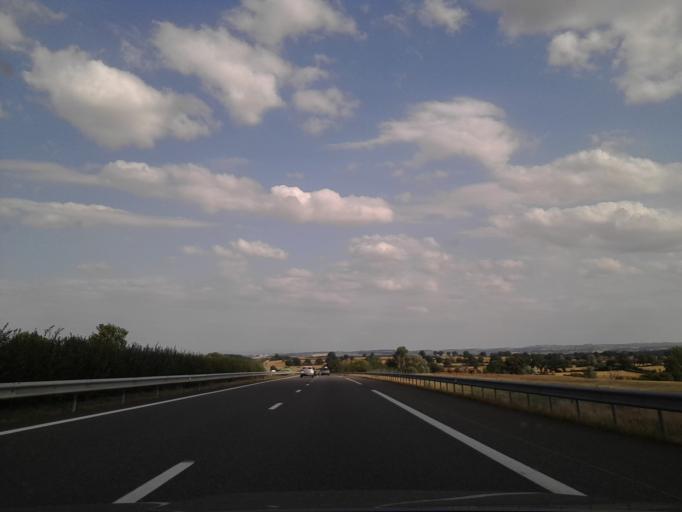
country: FR
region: Auvergne
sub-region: Departement de l'Allier
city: Bellenaves
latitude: 46.2656
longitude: 3.0636
